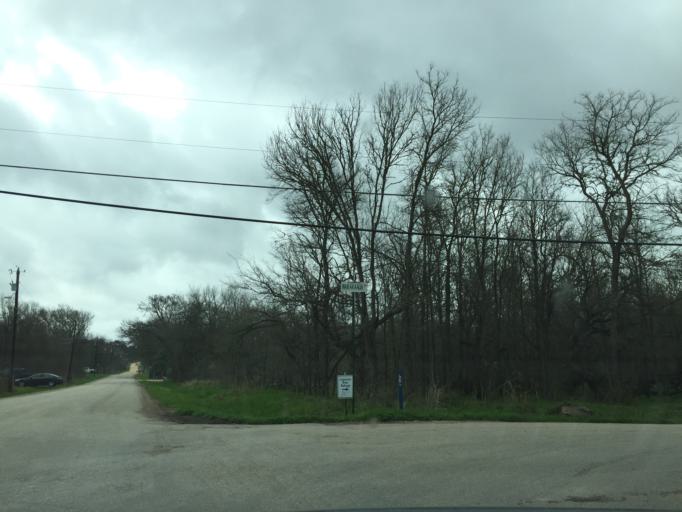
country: US
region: Texas
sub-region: Bastrop County
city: Bastrop
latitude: 30.0892
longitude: -97.3105
